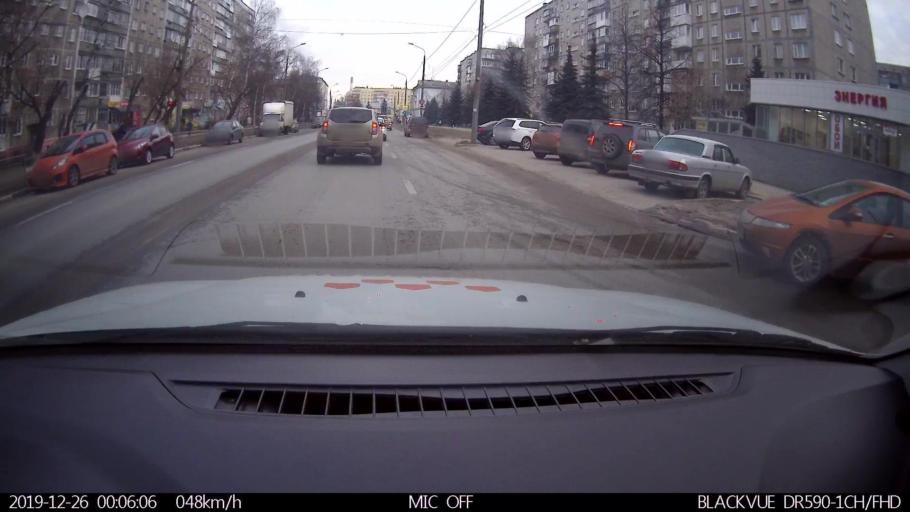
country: RU
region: Nizjnij Novgorod
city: Neklyudovo
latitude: 56.3491
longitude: 43.8616
